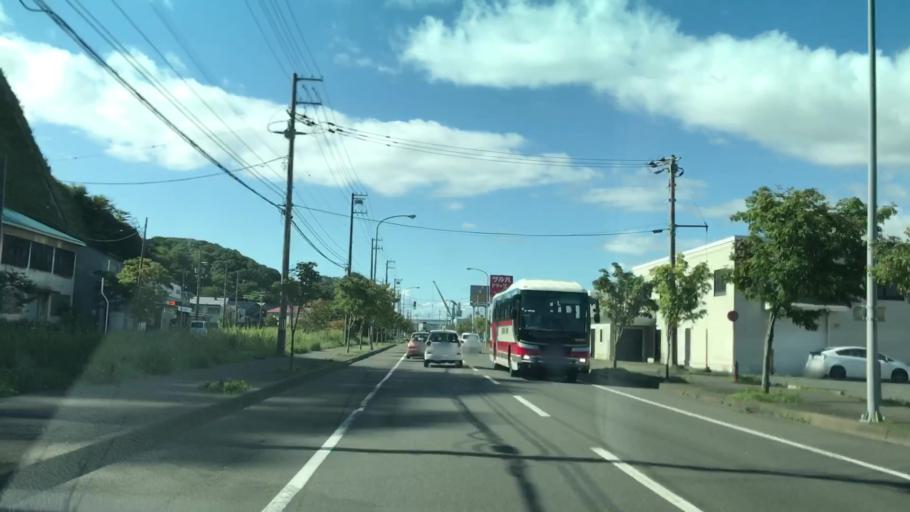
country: JP
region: Hokkaido
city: Muroran
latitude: 42.3308
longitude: 140.9655
